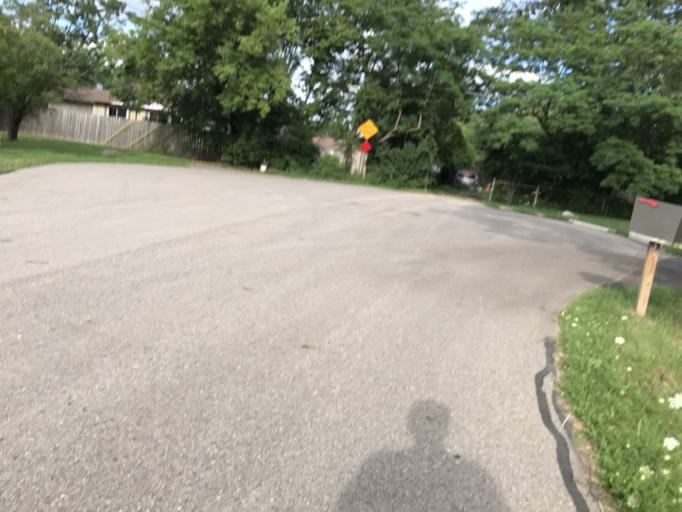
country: US
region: Michigan
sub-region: Oakland County
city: Farmington
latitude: 42.4684
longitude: -83.3525
